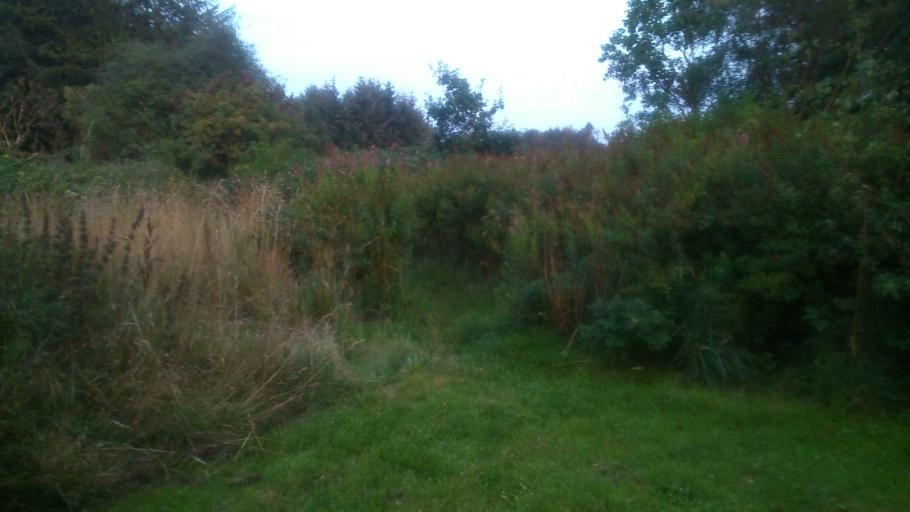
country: DK
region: Central Jutland
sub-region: Ringkobing-Skjern Kommune
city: Skjern
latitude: 56.0062
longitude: 8.4690
